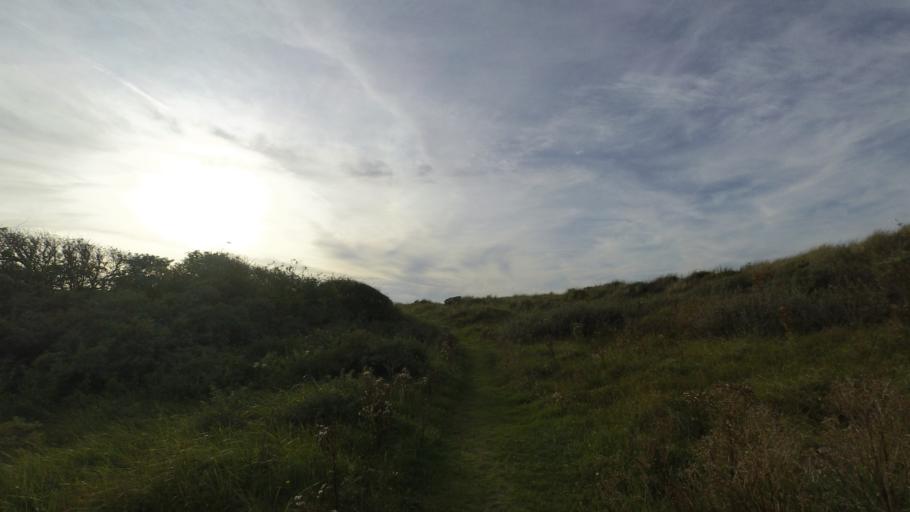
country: NL
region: Friesland
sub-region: Gemeente Ameland
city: Nes
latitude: 53.4600
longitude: 5.8124
